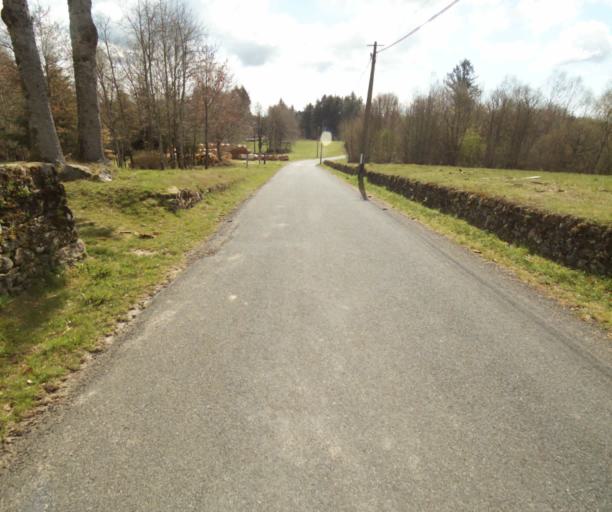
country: FR
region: Limousin
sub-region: Departement de la Correze
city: Argentat
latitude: 45.2438
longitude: 1.9525
